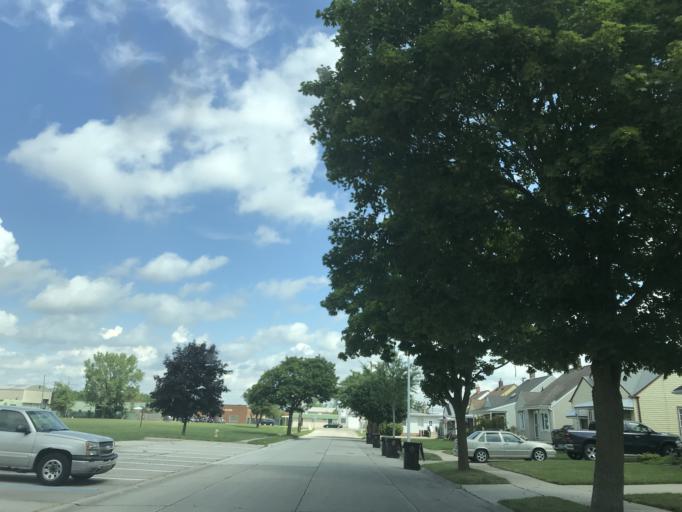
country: US
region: Michigan
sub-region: Wayne County
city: Riverview
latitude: 42.1692
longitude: -83.1771
